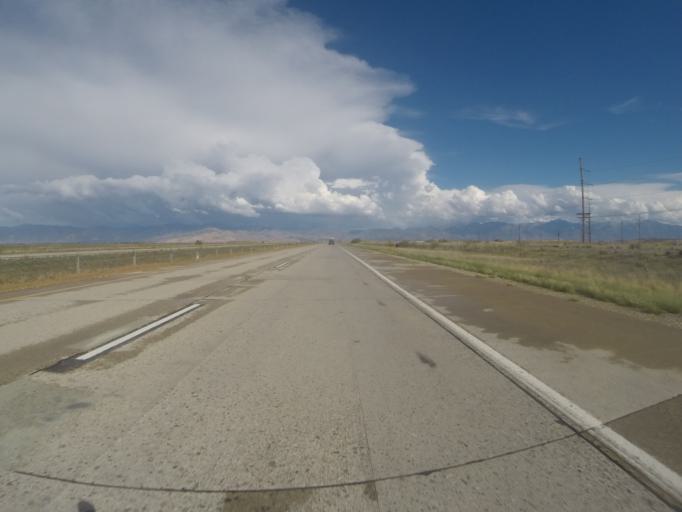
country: US
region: Utah
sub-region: Salt Lake County
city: Magna
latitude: 40.7708
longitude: -112.0958
